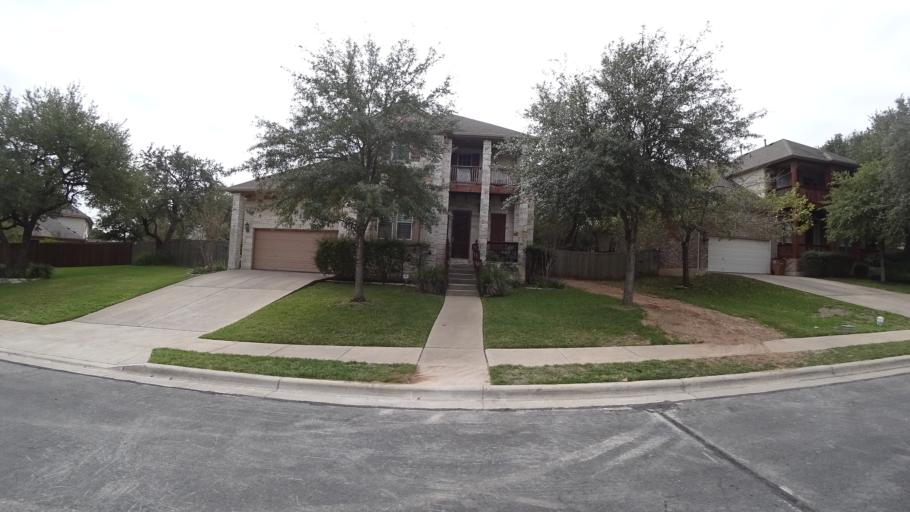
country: US
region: Texas
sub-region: Travis County
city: Shady Hollow
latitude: 30.1926
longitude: -97.9051
